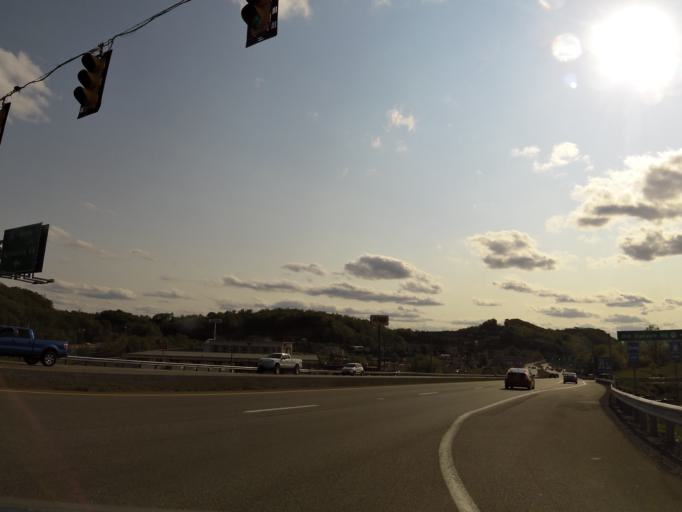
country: US
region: West Virginia
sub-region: Mercer County
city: Princeton
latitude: 37.3630
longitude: -81.0505
